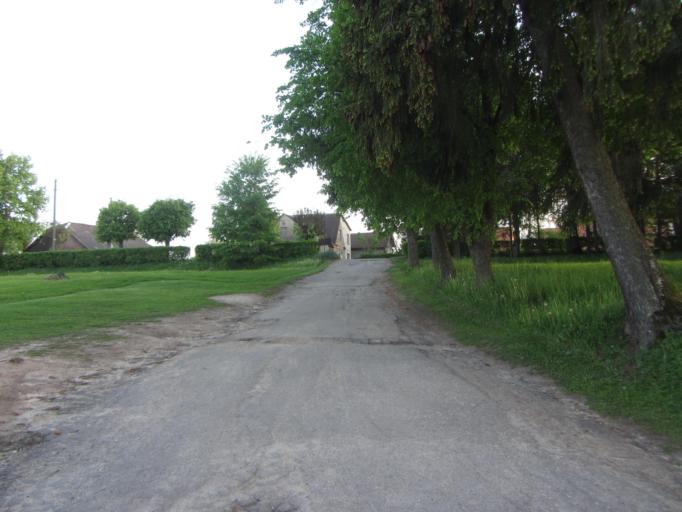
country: LT
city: Sirvintos
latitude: 55.0389
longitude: 24.9647
